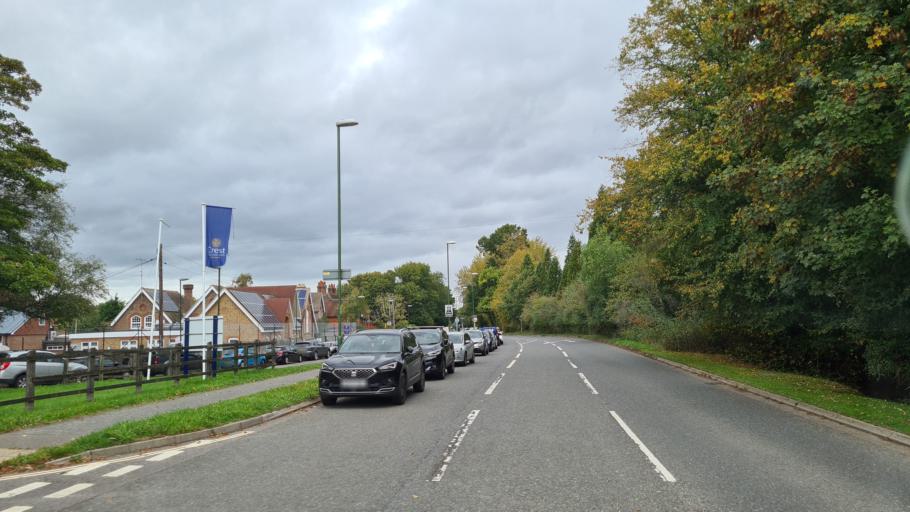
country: GB
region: England
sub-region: West Sussex
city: Broadfield
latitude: 51.0598
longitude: -0.1992
